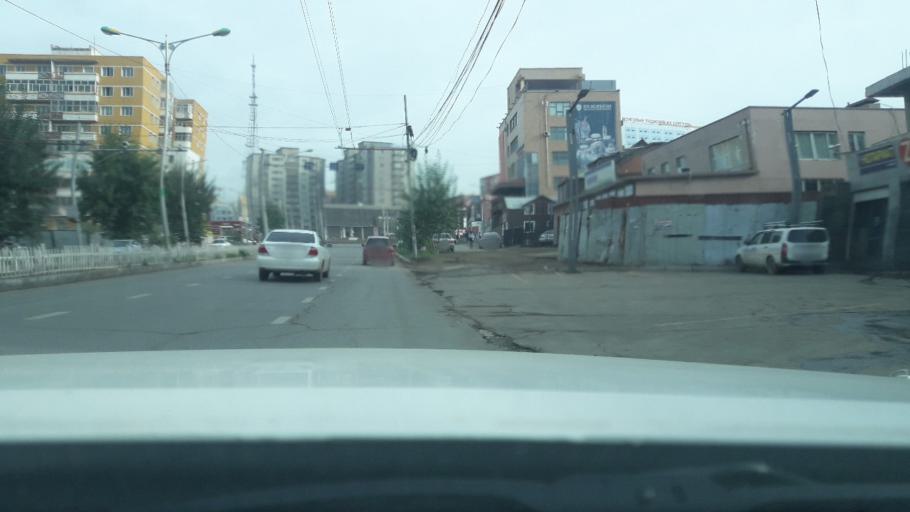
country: MN
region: Ulaanbaatar
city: Ulaanbaatar
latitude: 47.9215
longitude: 106.8906
